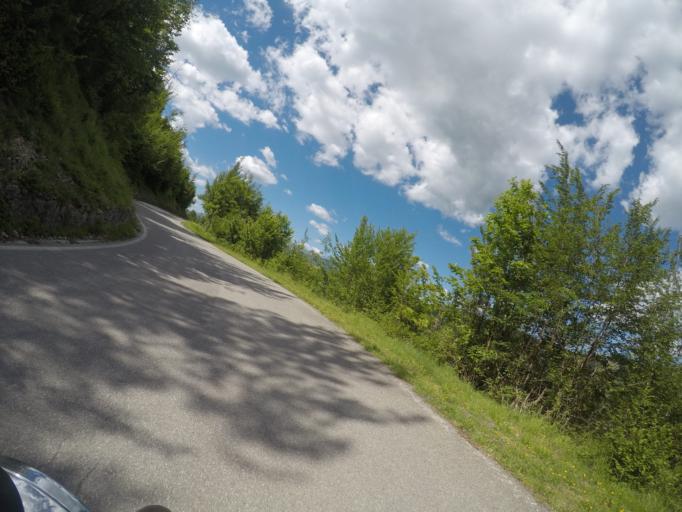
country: IT
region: Tuscany
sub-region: Provincia di Lucca
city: Minucciano
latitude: 44.1669
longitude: 10.2017
